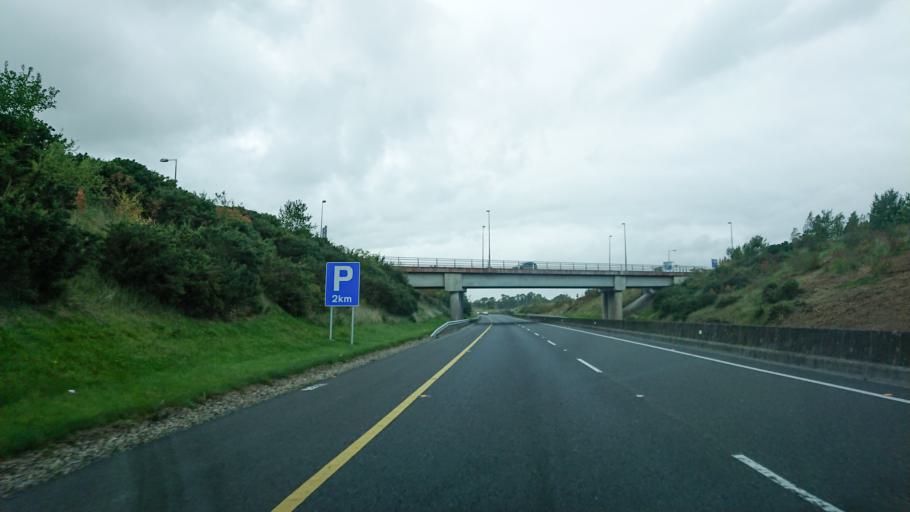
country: IE
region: Leinster
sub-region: Kilkenny
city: Mooncoin
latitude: 52.3728
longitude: -7.1667
